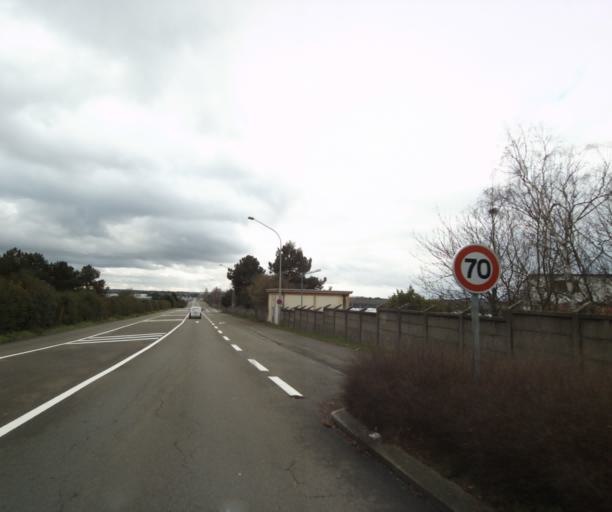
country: FR
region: Pays de la Loire
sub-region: Departement de la Sarthe
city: Arnage
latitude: 47.9563
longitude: 0.1980
